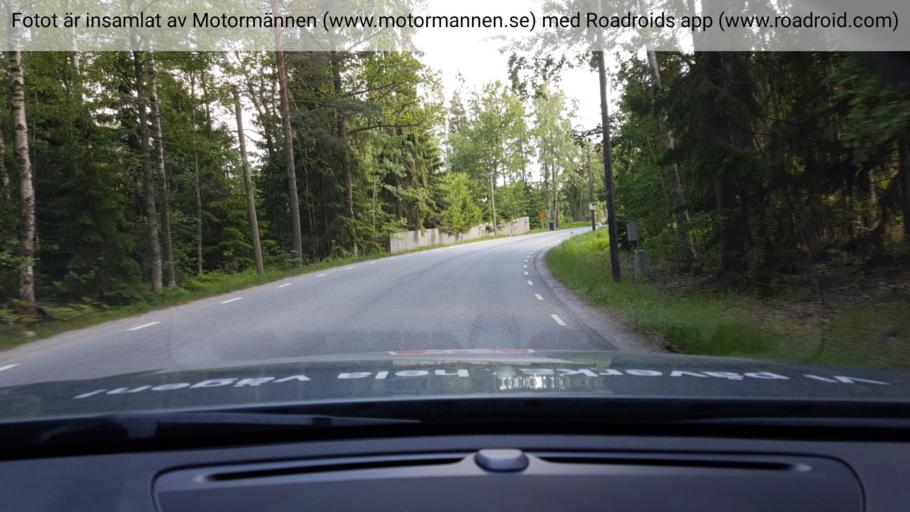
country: SE
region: Stockholm
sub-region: Varmdo Kommun
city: Mortnas
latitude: 59.2642
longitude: 18.4325
